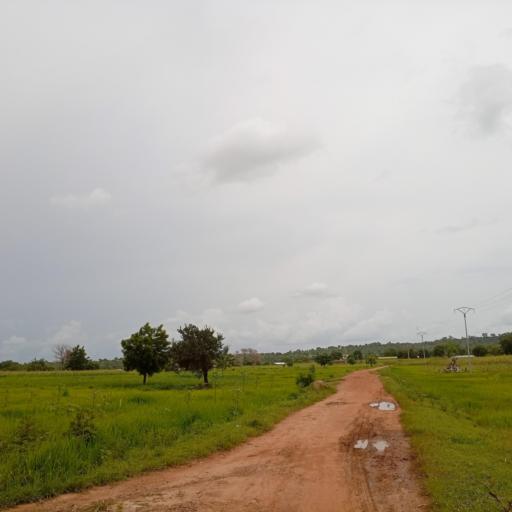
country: TG
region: Savanes
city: Dapaong
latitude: 10.8064
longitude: 0.0283
